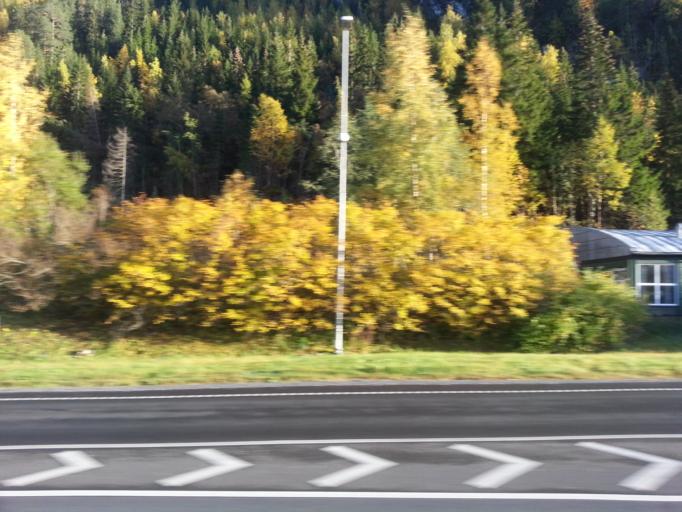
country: NO
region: Sor-Trondelag
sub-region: Malvik
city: Hommelvik
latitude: 63.4137
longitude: 10.8223
